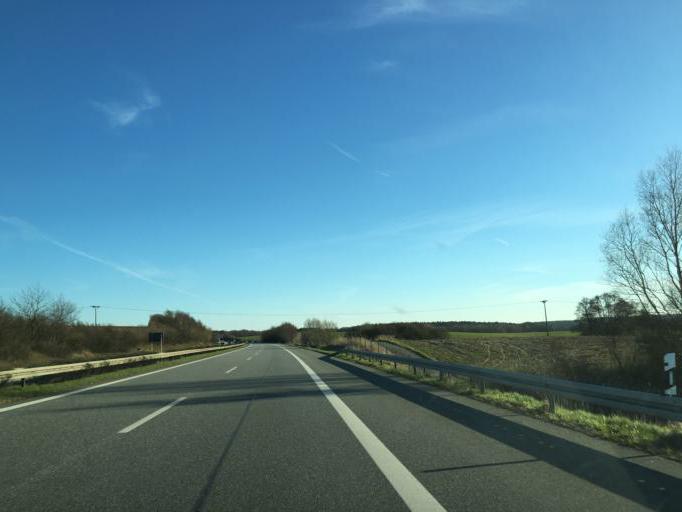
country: DE
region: Mecklenburg-Vorpommern
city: Muhl Rosin
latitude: 53.8111
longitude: 12.2978
